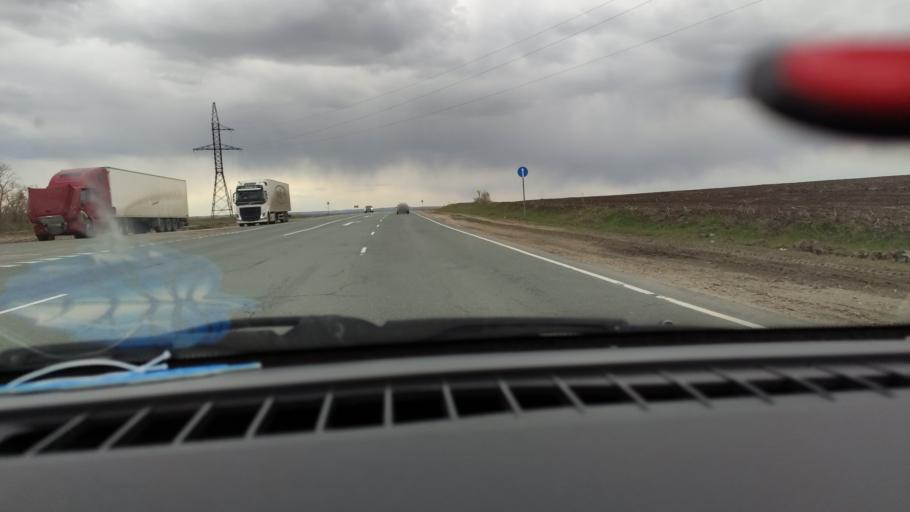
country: RU
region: Saratov
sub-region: Saratovskiy Rayon
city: Saratov
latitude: 51.7443
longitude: 46.0499
